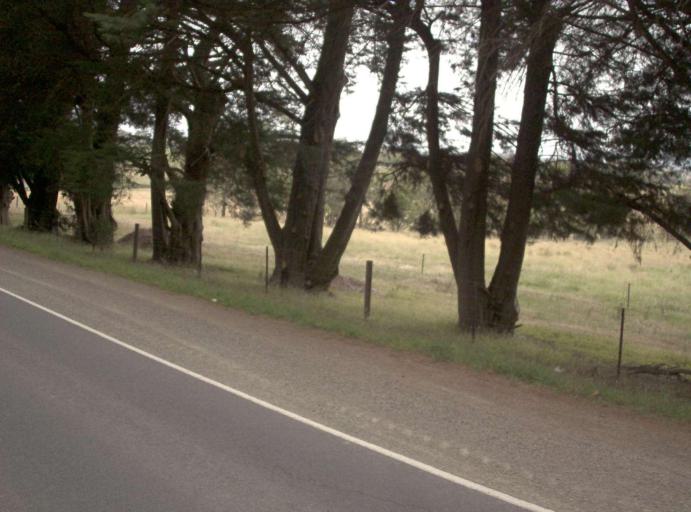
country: AU
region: Victoria
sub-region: Yarra Ranges
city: Lilydale
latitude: -37.7177
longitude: 145.3798
